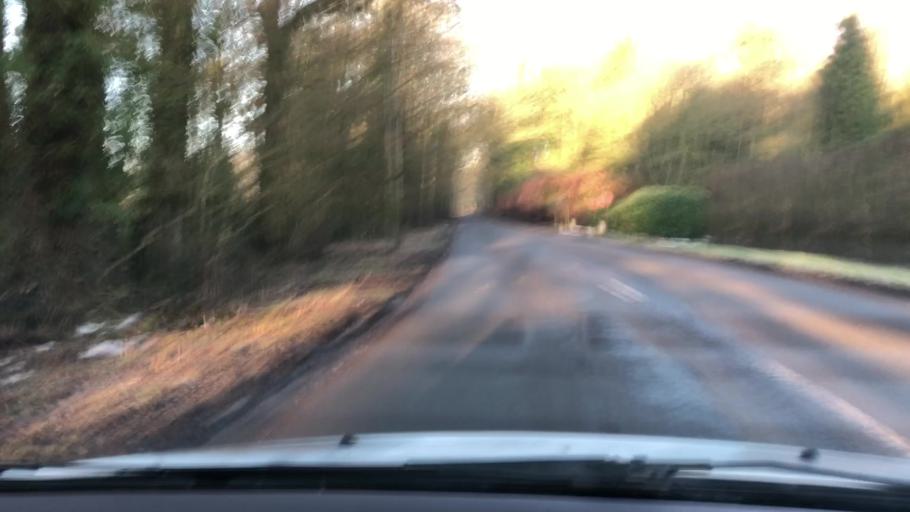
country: GB
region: England
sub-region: Hampshire
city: Alton
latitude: 51.1899
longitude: -1.0051
